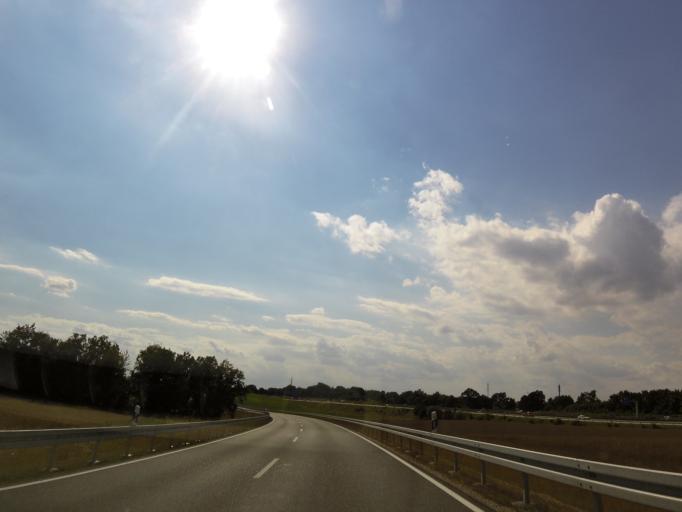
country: DE
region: Saxony
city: Pfaffroda
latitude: 50.8387
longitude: 12.5047
